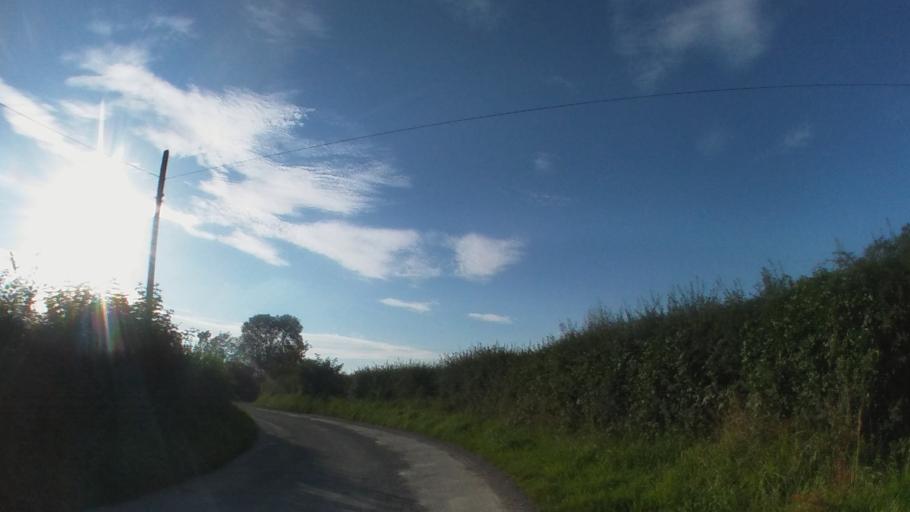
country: IE
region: Leinster
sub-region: Kilkenny
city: Kilkenny
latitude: 52.6949
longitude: -7.1911
